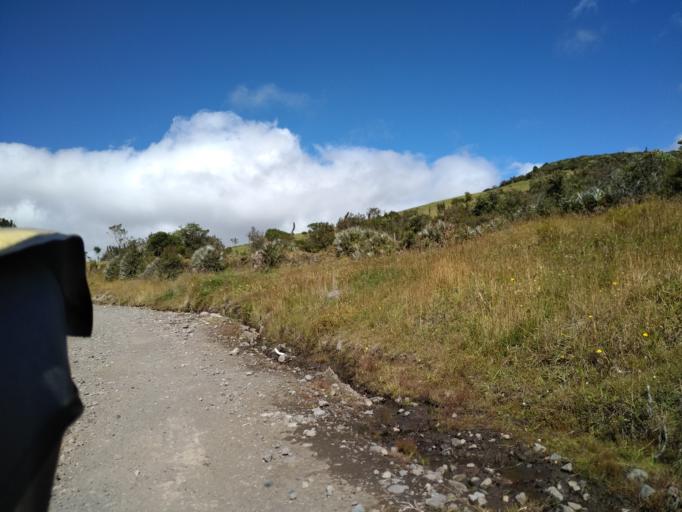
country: EC
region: Pichincha
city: Machachi
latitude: -0.5337
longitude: -78.4816
